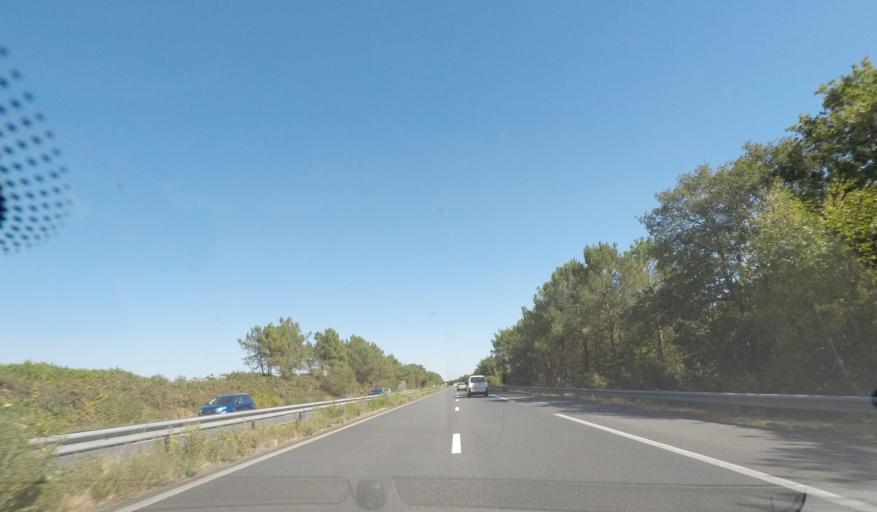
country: FR
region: Pays de la Loire
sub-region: Departement de la Loire-Atlantique
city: La Chapelle-des-Marais
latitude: 47.4923
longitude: -2.2396
